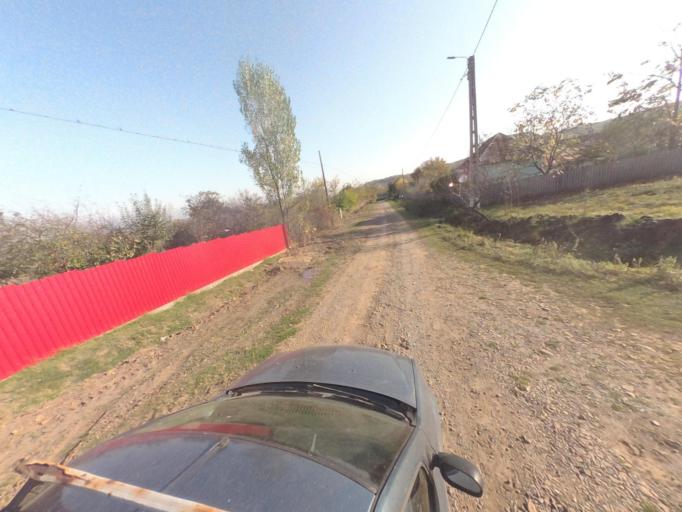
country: RO
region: Vaslui
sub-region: Comuna Bacesti
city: Bacesti
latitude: 46.8739
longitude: 27.1964
